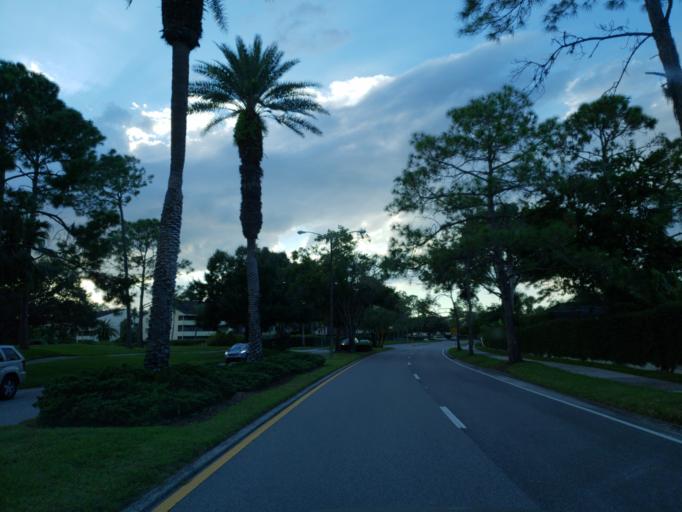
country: US
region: Florida
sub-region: Hillsborough County
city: Carrollwood Village
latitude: 28.0708
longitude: -82.5185
